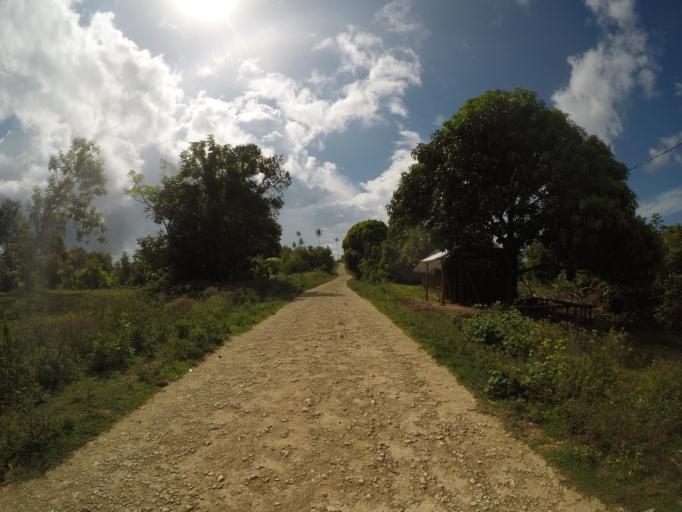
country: TZ
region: Pemba South
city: Mtambile
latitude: -5.3488
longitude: 39.6949
